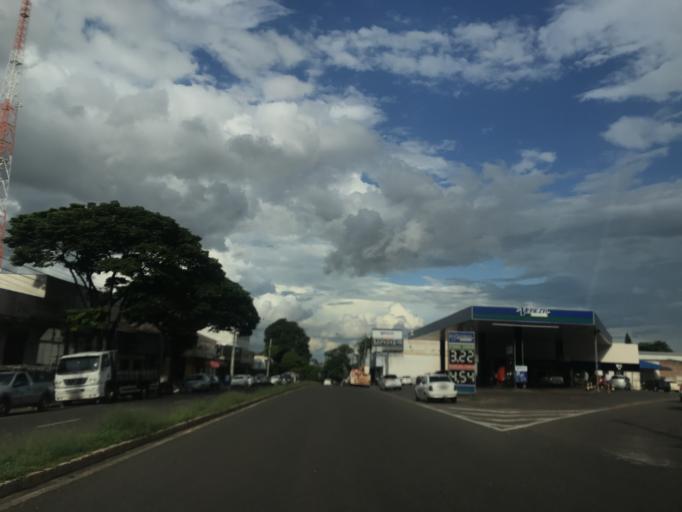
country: BR
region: Parana
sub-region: Maringa
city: Maringa
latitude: -23.4262
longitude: -51.9635
